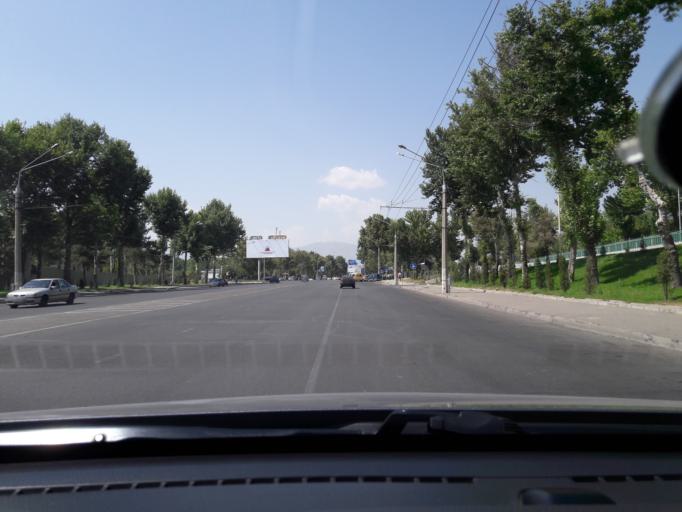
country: TJ
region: Dushanbe
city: Dushanbe
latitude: 38.5699
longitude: 68.7548
